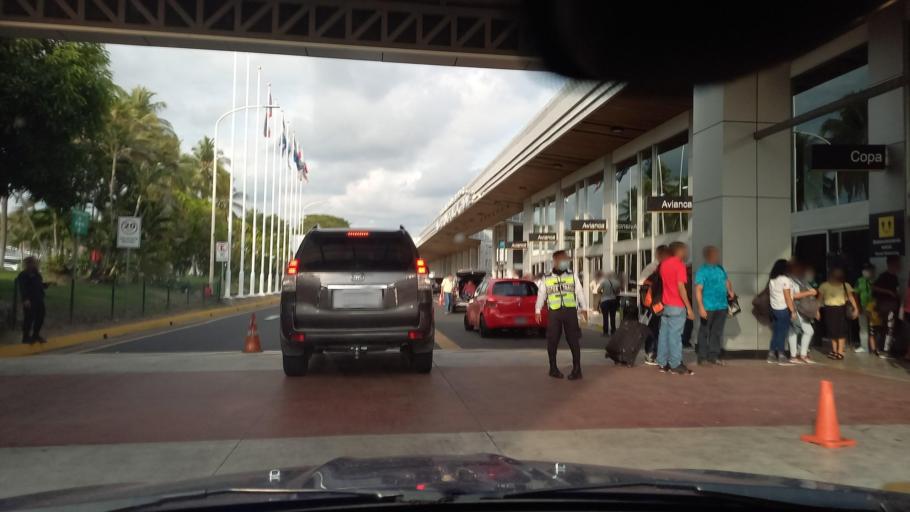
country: SV
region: La Paz
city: El Rosario
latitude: 13.4450
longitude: -89.0577
